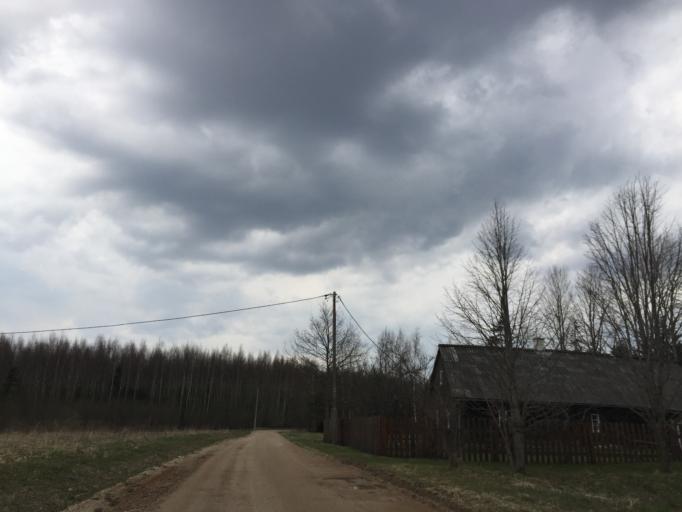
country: EE
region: Vorumaa
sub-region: Antsla vald
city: Vana-Antsla
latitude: 57.9434
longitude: 26.7195
